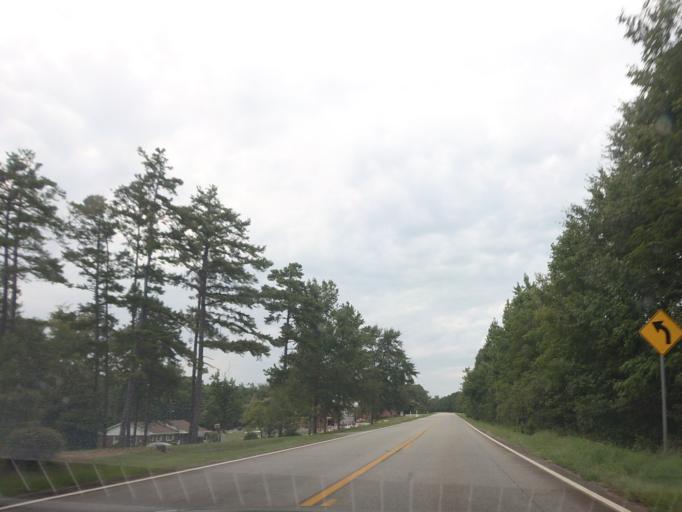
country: US
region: Georgia
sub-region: Twiggs County
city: Jeffersonville
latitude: 32.7302
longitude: -83.4187
